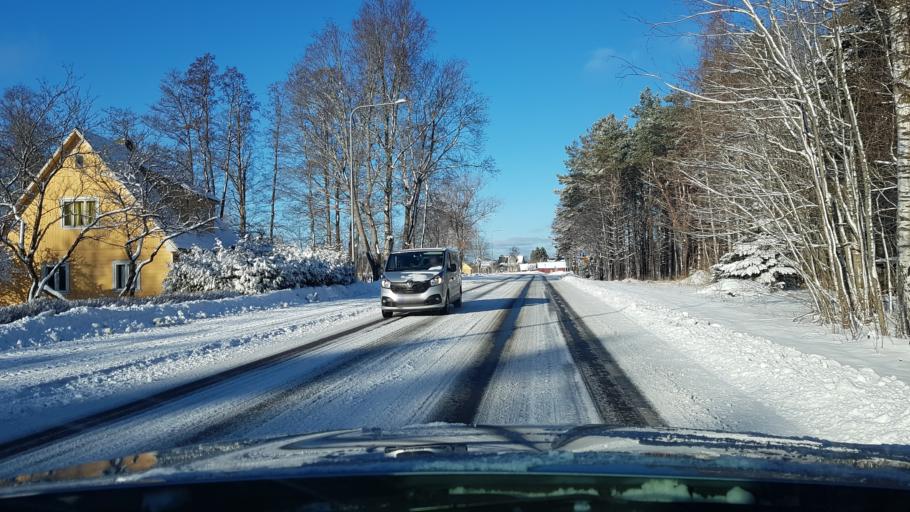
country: EE
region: Hiiumaa
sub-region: Kaerdla linn
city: Kardla
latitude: 58.9833
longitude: 22.7575
